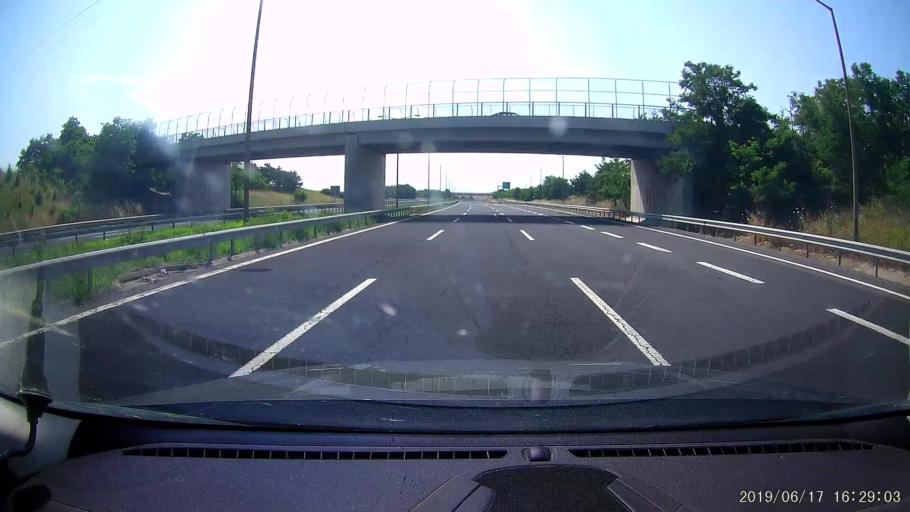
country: TR
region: Tekirdag
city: Beyazkoy
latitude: 41.3317
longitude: 27.6931
